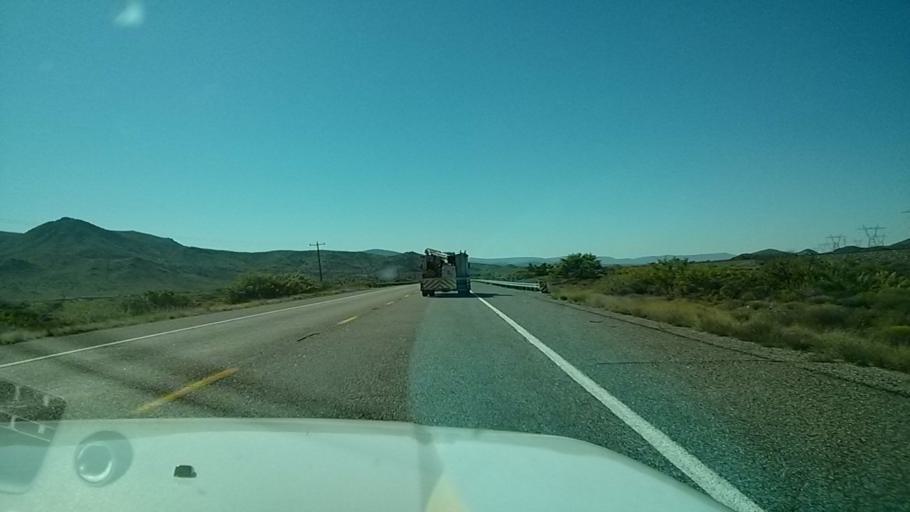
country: US
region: Arizona
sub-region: Mohave County
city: New Kingman-Butler
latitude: 35.3951
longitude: -113.7502
